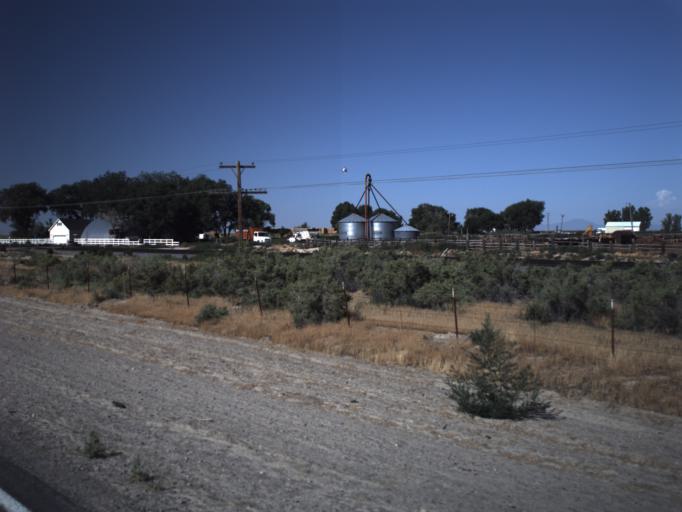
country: US
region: Utah
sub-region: Millard County
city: Delta
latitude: 39.5405
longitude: -112.3631
